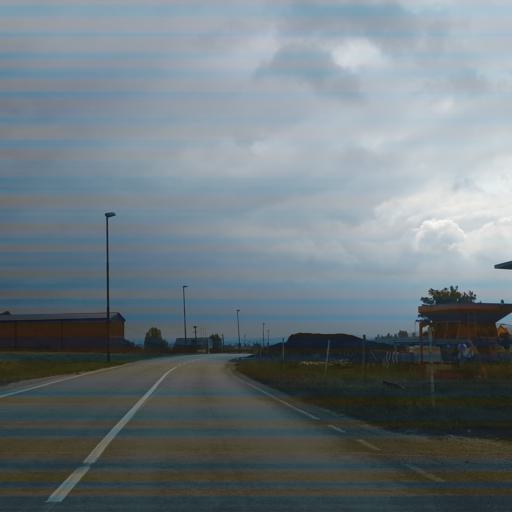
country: RS
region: Central Serbia
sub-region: Nisavski Okrug
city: Razanj
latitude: 43.6816
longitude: 21.5465
